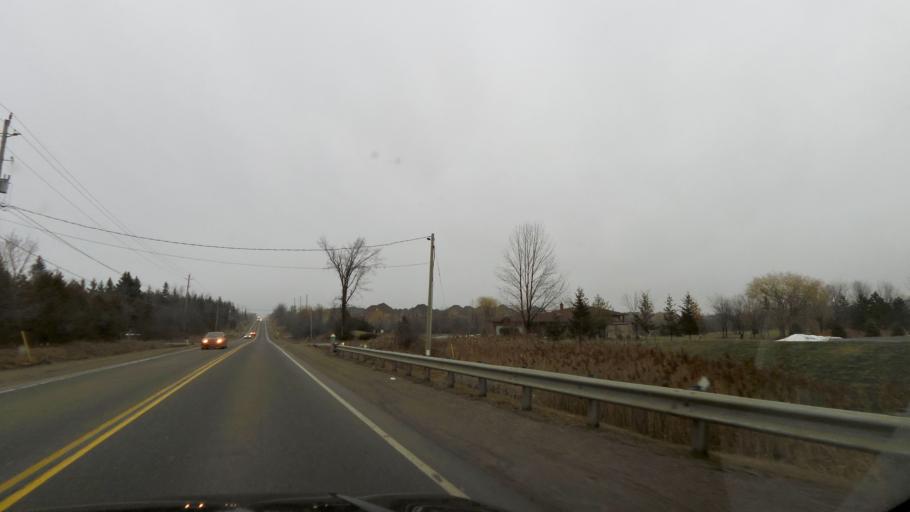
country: CA
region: Ontario
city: Brampton
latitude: 43.8020
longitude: -79.7472
